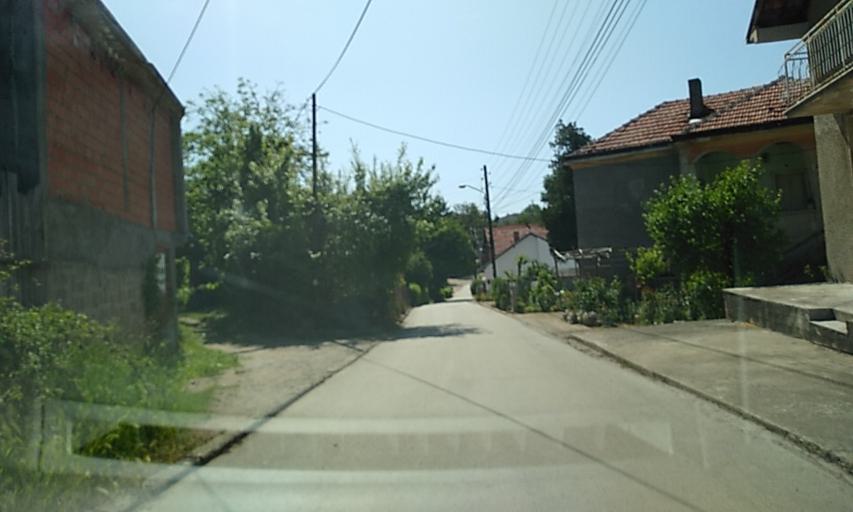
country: RS
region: Central Serbia
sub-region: Nisavski Okrug
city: Niska Banja
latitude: 43.2953
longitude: 22.0105
